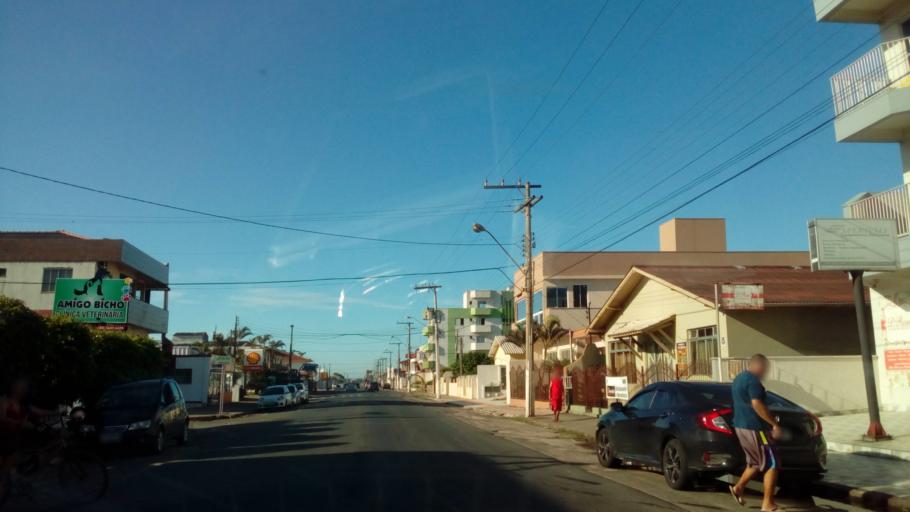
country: BR
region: Santa Catarina
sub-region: Laguna
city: Laguna
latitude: -28.4907
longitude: -48.7716
